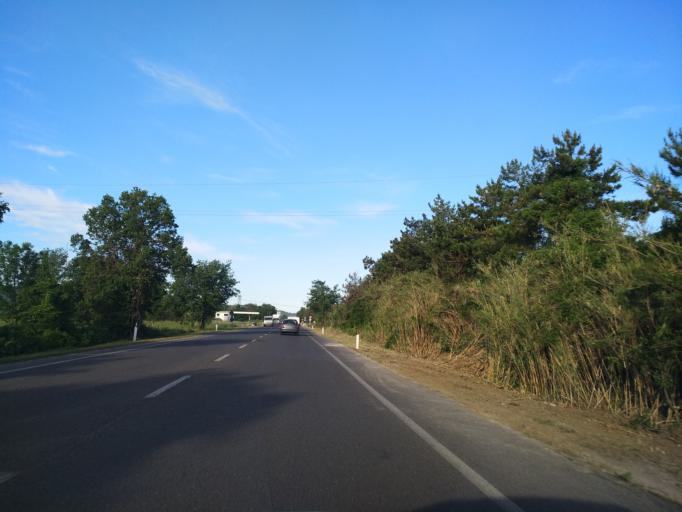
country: IT
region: The Marches
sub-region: Provincia di Pesaro e Urbino
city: Villa Ceccolini
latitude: 43.8815
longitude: 12.8548
